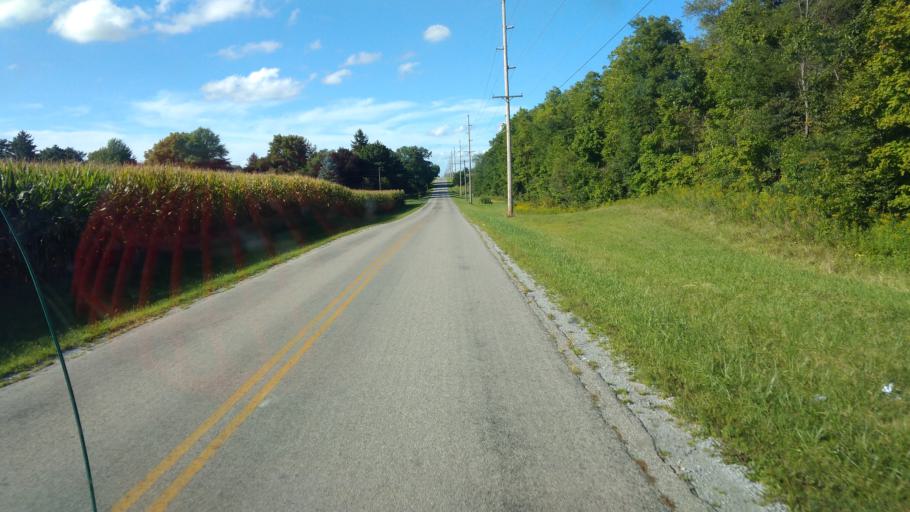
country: US
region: Ohio
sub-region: Hardin County
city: Kenton
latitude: 40.7134
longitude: -83.6533
